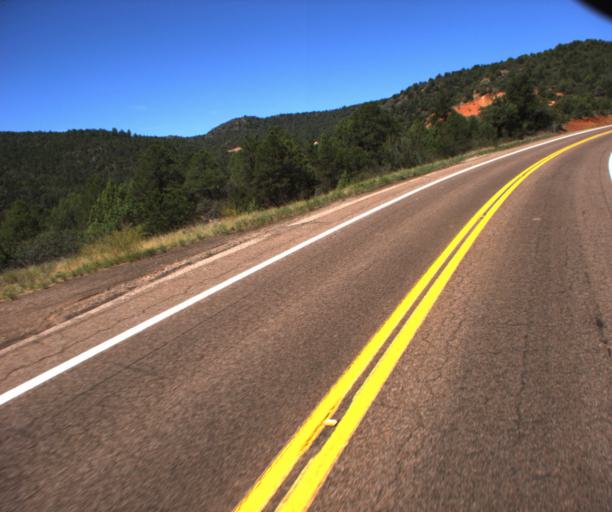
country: US
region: Arizona
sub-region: Navajo County
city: Cibecue
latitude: 33.9316
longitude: -110.3437
